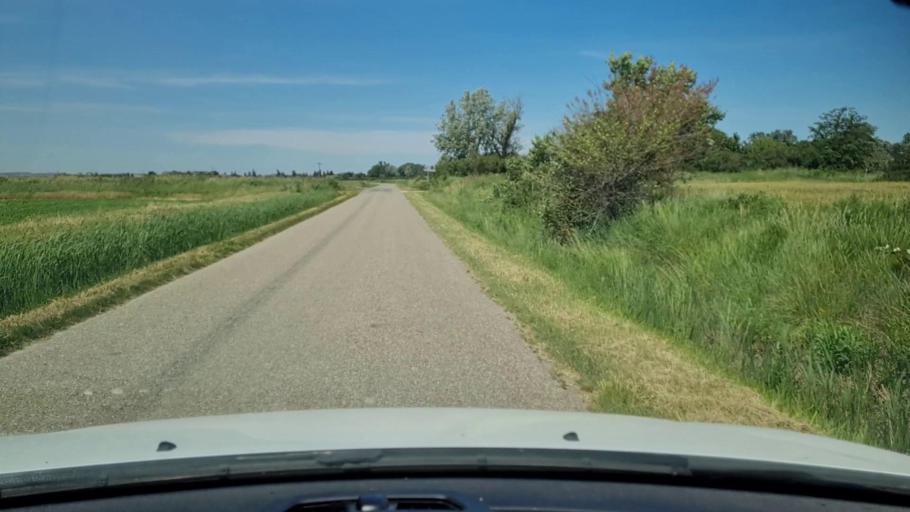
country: FR
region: Languedoc-Roussillon
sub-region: Departement du Gard
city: Saint-Gilles
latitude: 43.6158
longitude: 4.4259
